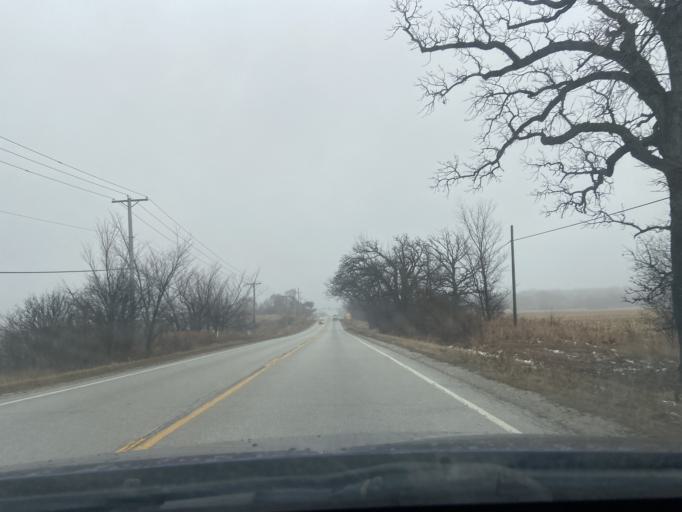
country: US
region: Illinois
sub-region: Lake County
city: Round Lake
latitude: 42.3163
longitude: -88.1162
